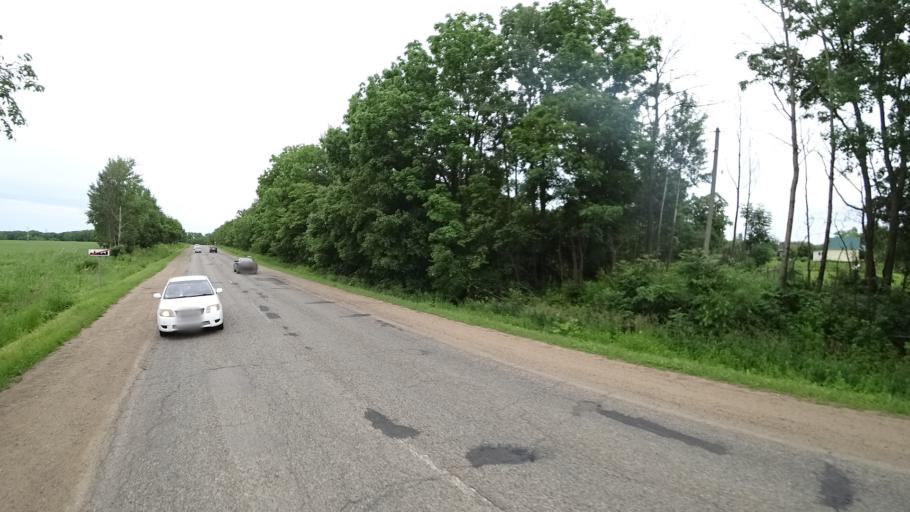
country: RU
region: Primorskiy
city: Novosysoyevka
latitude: 44.1843
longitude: 133.3518
